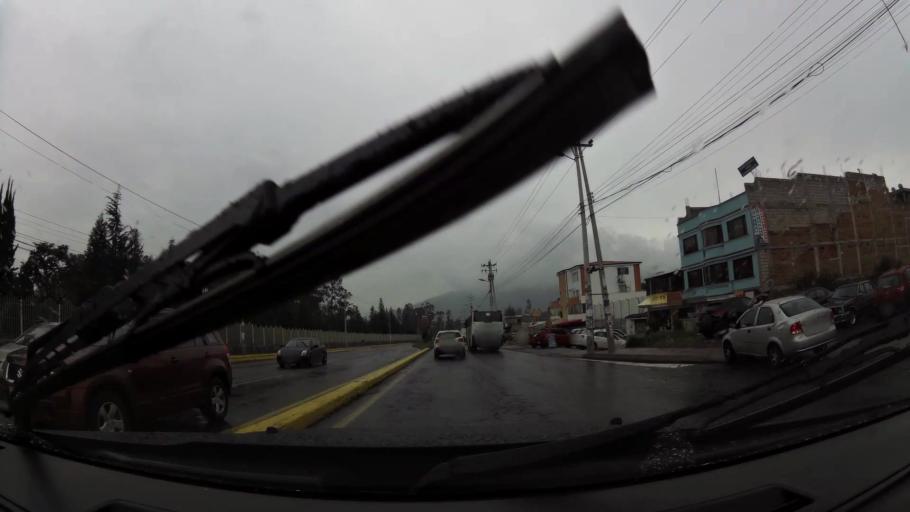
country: EC
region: Pichincha
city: Sangolqui
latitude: -0.3145
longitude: -78.4420
